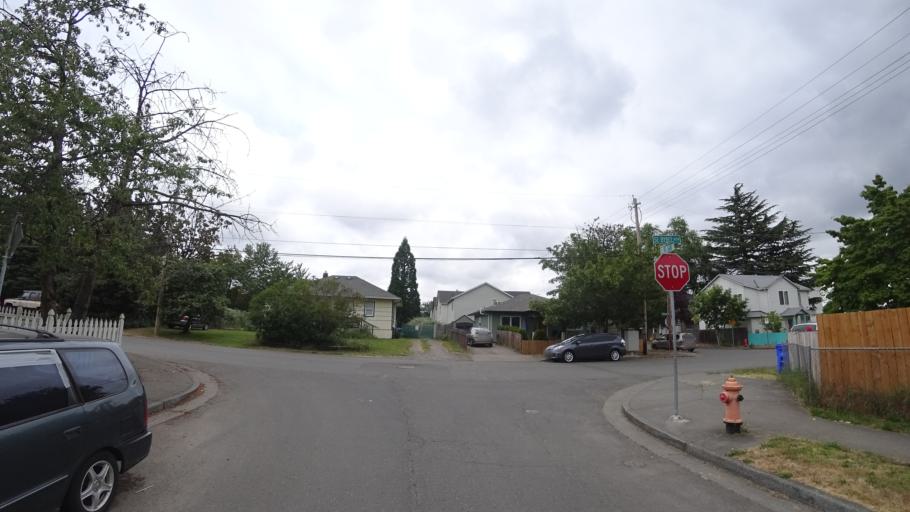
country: US
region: Oregon
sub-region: Multnomah County
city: Lents
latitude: 45.4719
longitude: -122.5807
